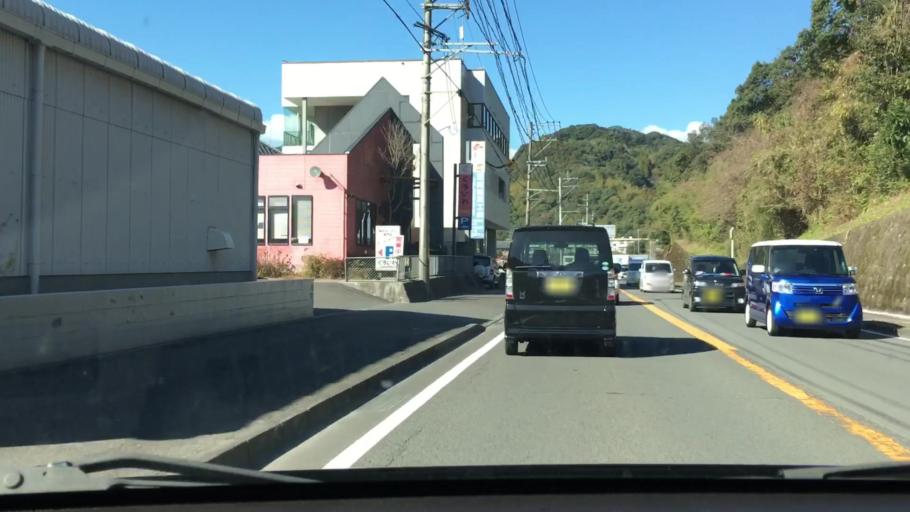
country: JP
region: Kagoshima
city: Kagoshima-shi
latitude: 31.6400
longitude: 130.5166
